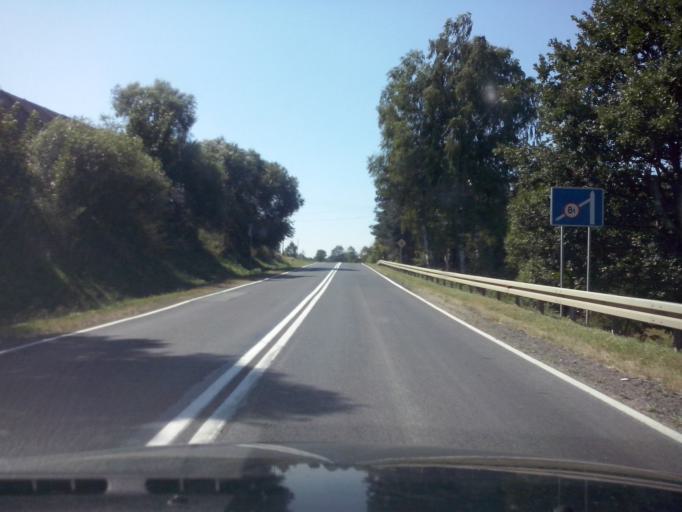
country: PL
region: Swietokrzyskie
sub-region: Powiat kielecki
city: Bieliny
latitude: 50.8202
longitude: 20.9286
